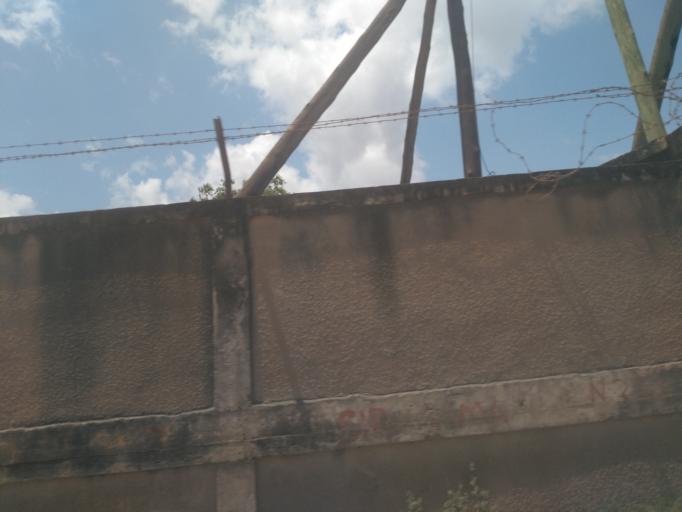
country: TZ
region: Dar es Salaam
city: Dar es Salaam
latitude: -6.8391
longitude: 39.2878
